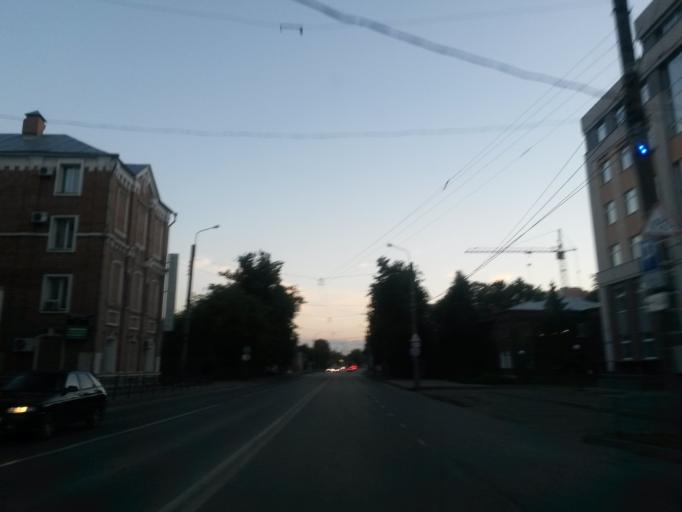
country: RU
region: Ivanovo
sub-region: Gorod Ivanovo
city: Ivanovo
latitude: 56.9944
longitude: 40.9709
